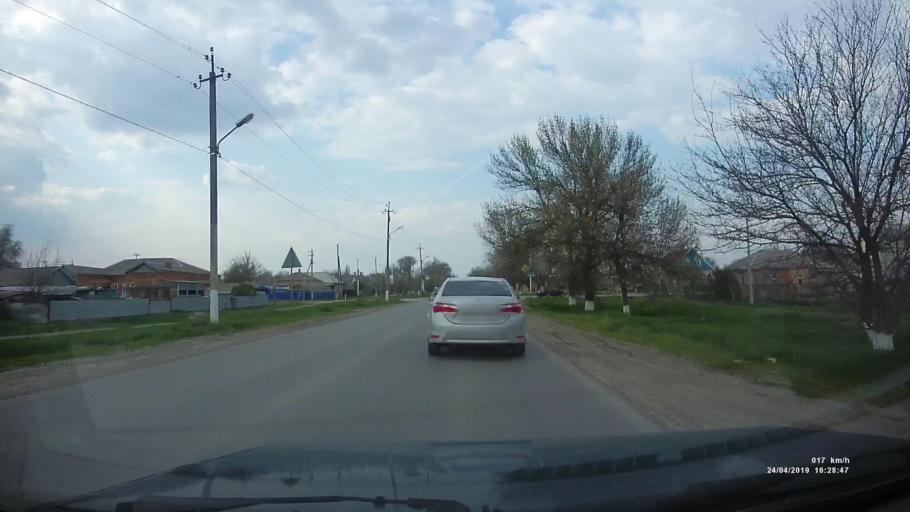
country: RU
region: Rostov
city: Orlovskiy
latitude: 46.8662
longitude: 42.0342
